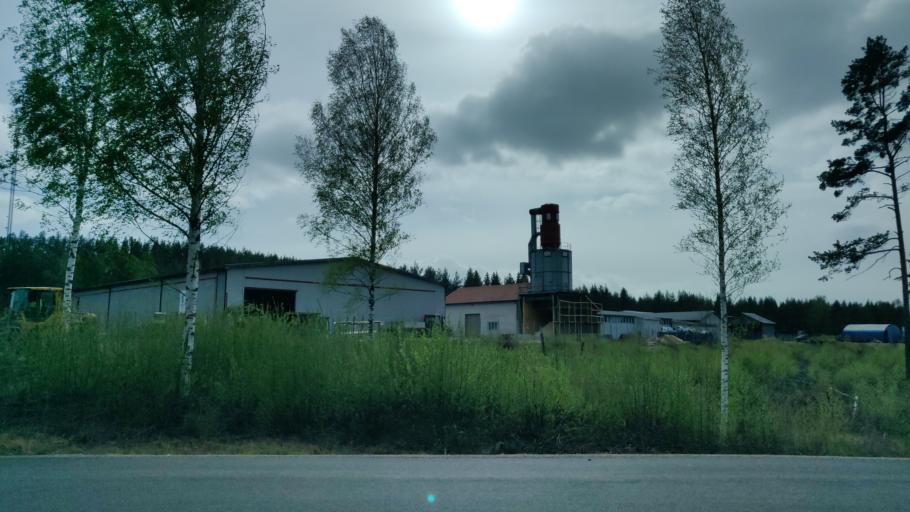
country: SE
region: Vaermland
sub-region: Forshaga Kommun
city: Deje
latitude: 59.6196
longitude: 13.4475
